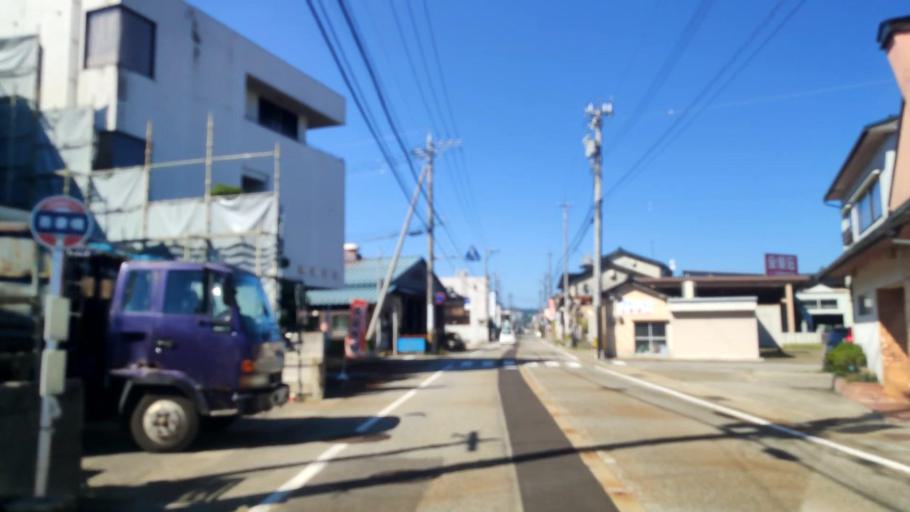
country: JP
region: Ishikawa
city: Nanao
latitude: 37.4377
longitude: 137.2654
